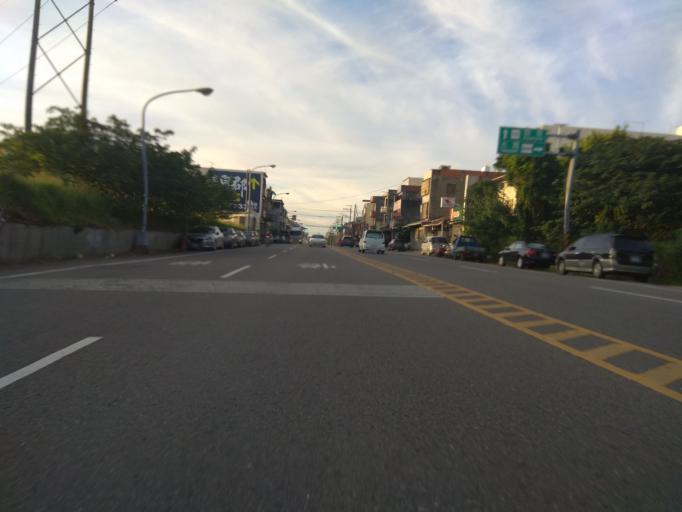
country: TW
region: Taiwan
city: Taoyuan City
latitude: 24.9785
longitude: 121.1945
